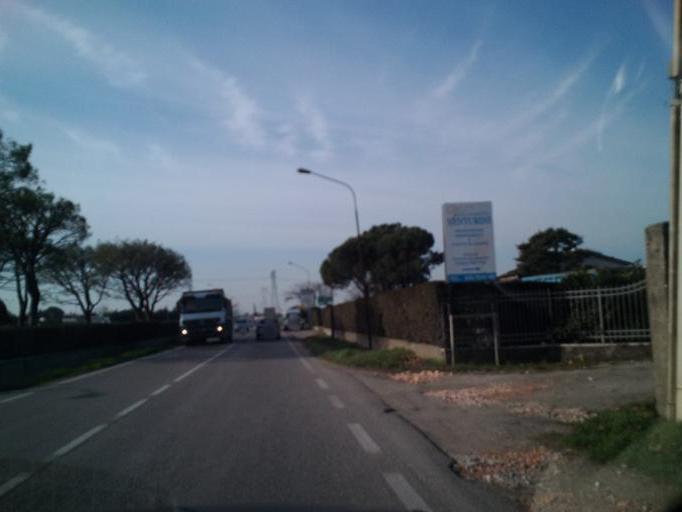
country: IT
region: Veneto
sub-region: Provincia di Verona
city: Mozzecane
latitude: 45.3180
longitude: 10.8268
